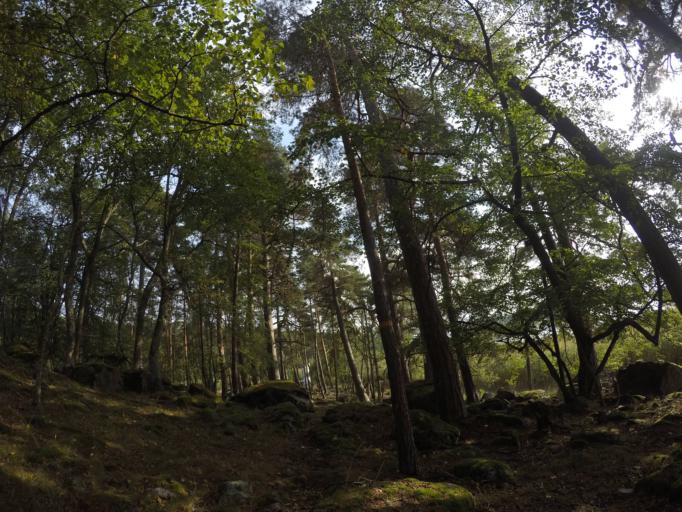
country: SE
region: Vaestmanland
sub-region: Hallstahammars Kommun
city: Kolback
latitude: 59.4715
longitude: 16.2141
